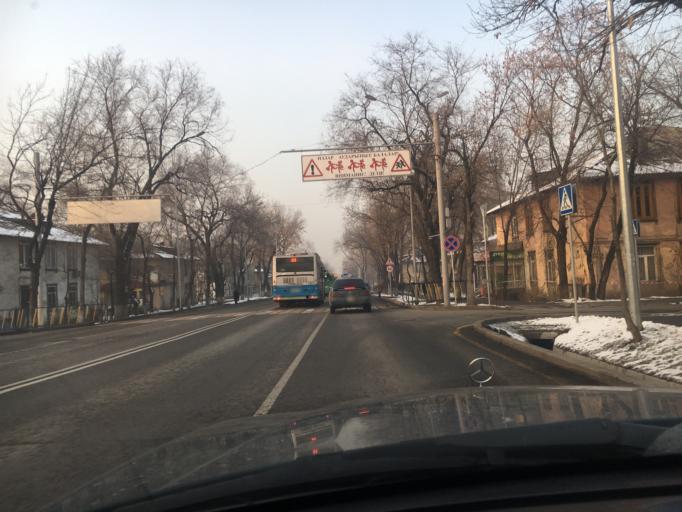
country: KZ
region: Almaty Qalasy
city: Almaty
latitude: 43.2083
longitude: 76.8790
